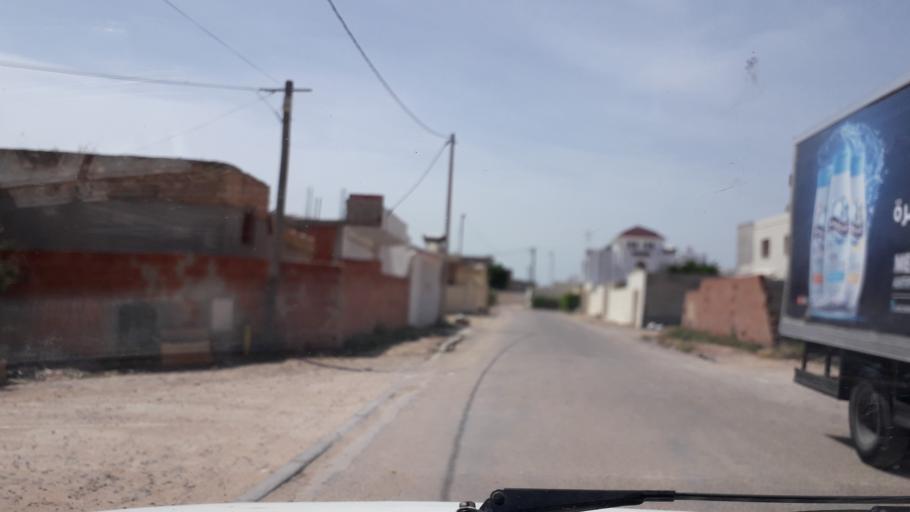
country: TN
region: Safaqis
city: Al Qarmadah
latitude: 34.8002
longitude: 10.7626
